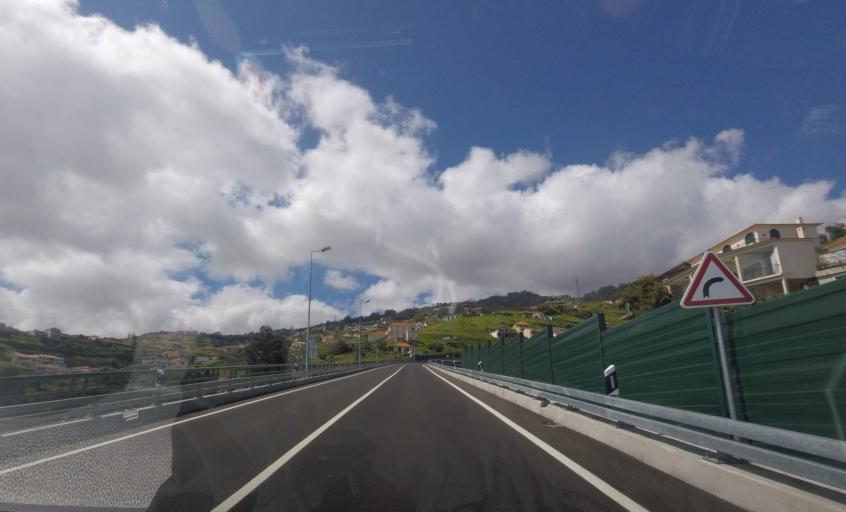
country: PT
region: Madeira
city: Camara de Lobos
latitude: 32.6718
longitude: -16.9741
